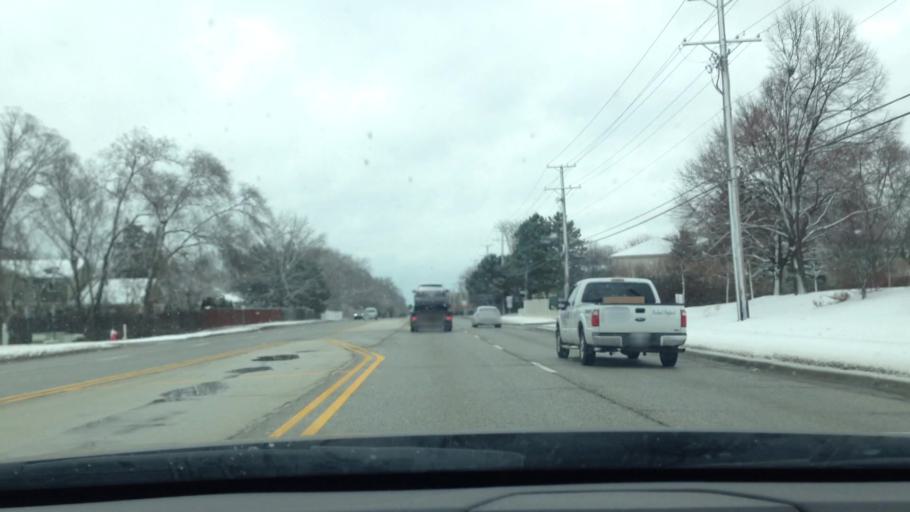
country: US
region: Illinois
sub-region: Cook County
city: Northbrook
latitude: 42.1057
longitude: -87.8464
